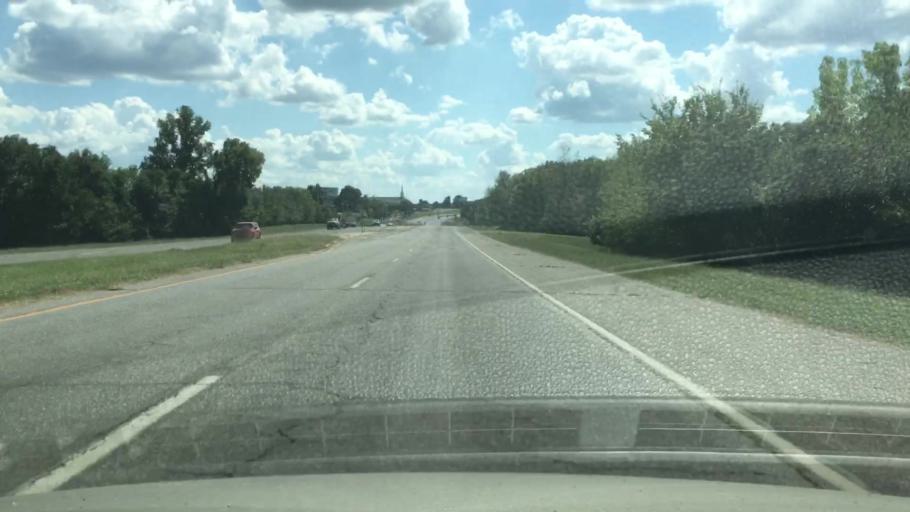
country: US
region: Oklahoma
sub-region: Cherokee County
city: Tahlequah
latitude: 35.9174
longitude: -94.9559
